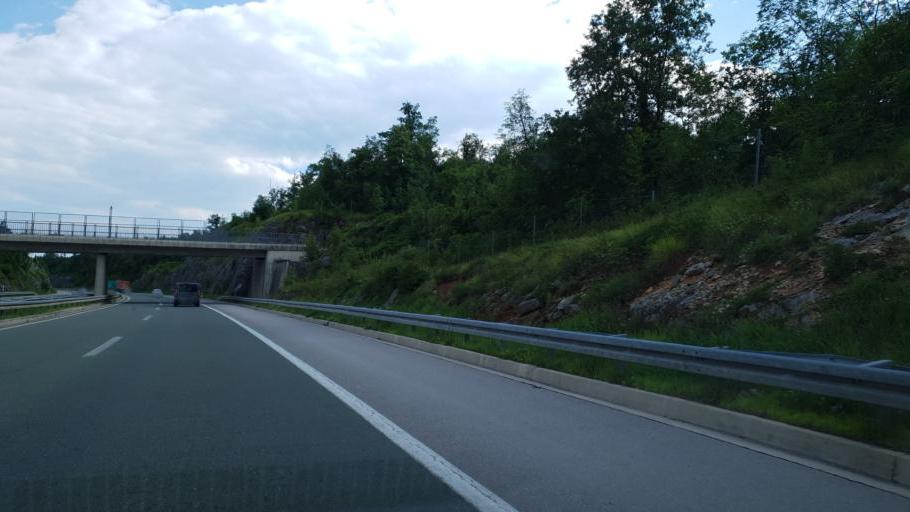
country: HR
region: Primorsko-Goranska
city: Matulji
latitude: 45.3906
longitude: 14.3003
